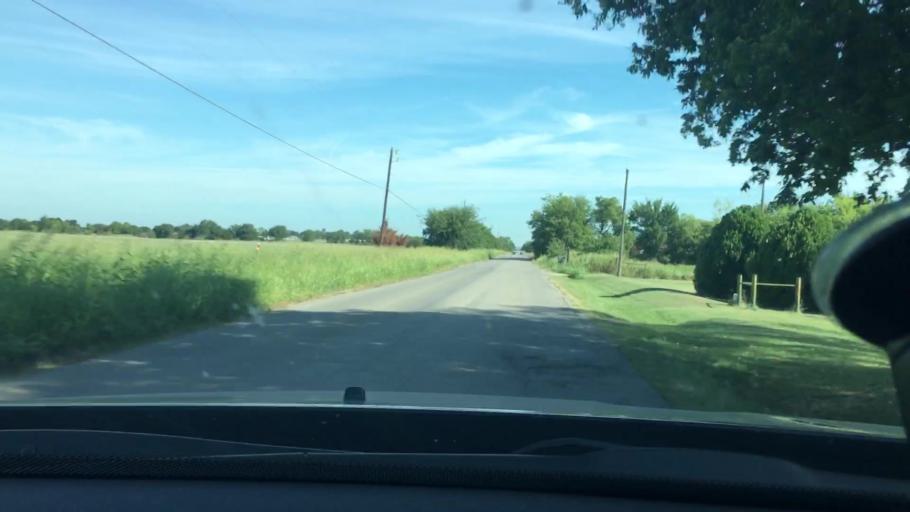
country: US
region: Oklahoma
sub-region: Carter County
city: Lone Grove
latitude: 34.1929
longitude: -97.2475
